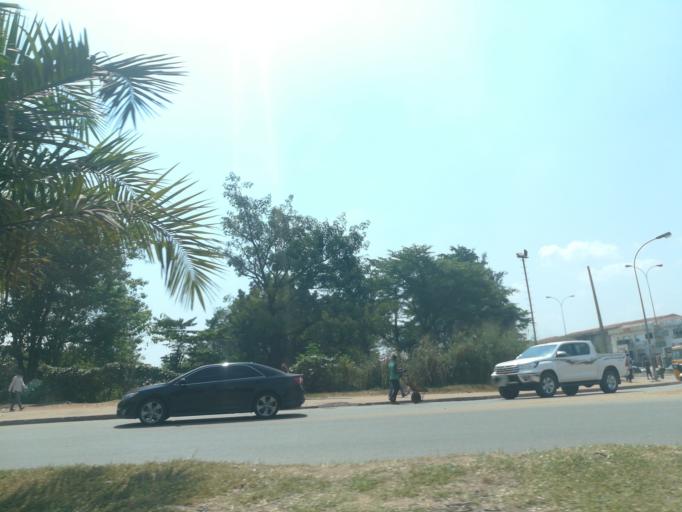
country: NG
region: Abuja Federal Capital Territory
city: Abuja
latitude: 9.0666
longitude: 7.4354
